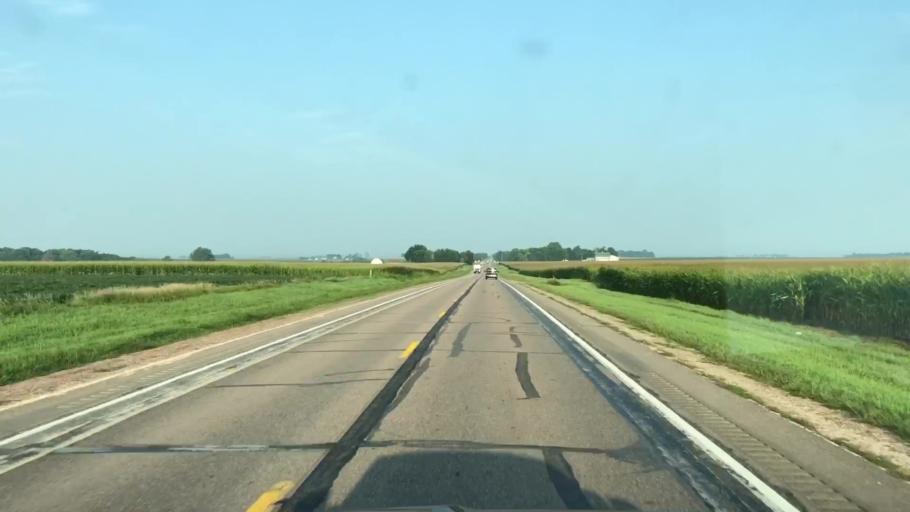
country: US
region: Iowa
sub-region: O'Brien County
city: Sheldon
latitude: 43.1860
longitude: -95.9103
